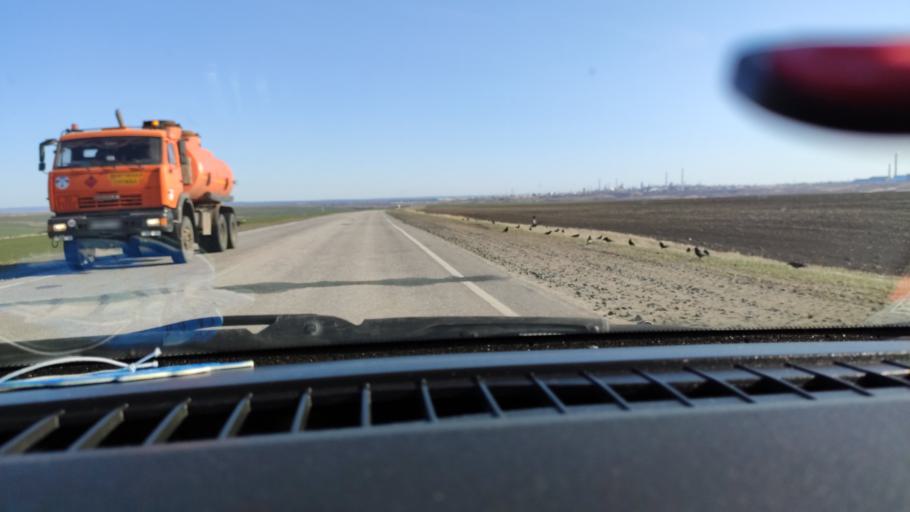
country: RU
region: Samara
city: Varlamovo
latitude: 53.0378
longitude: 48.3376
